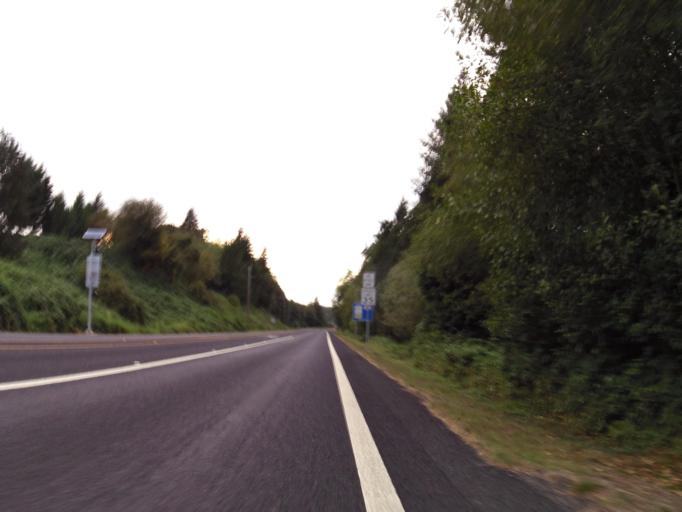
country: US
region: Washington
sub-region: Wahkiakum County
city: Cathlamet
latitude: 46.2022
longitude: -123.3773
